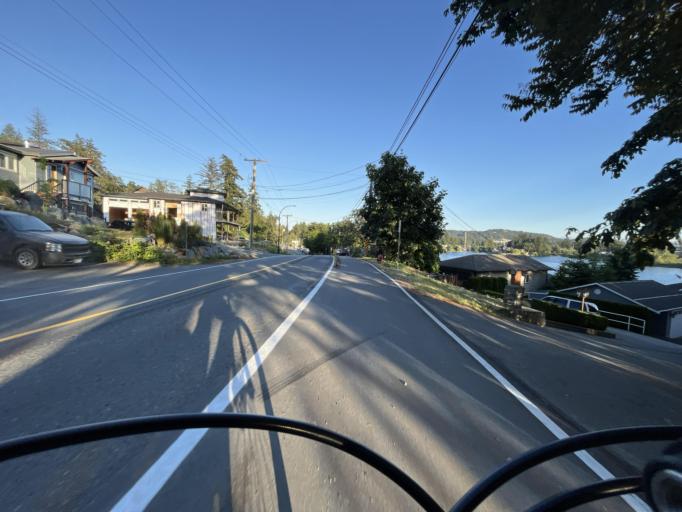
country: CA
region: British Columbia
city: Langford
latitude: 48.4510
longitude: -123.5277
